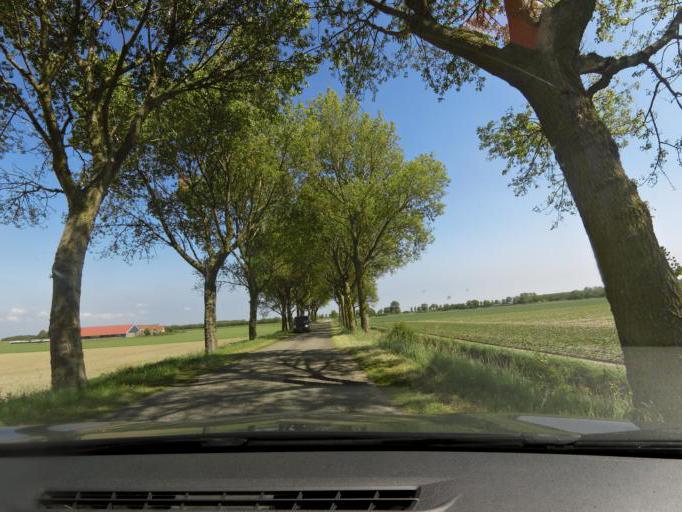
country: NL
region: South Holland
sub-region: Gemeente Goeree-Overflakkee
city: Dirksland
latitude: 51.7854
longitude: 4.1043
